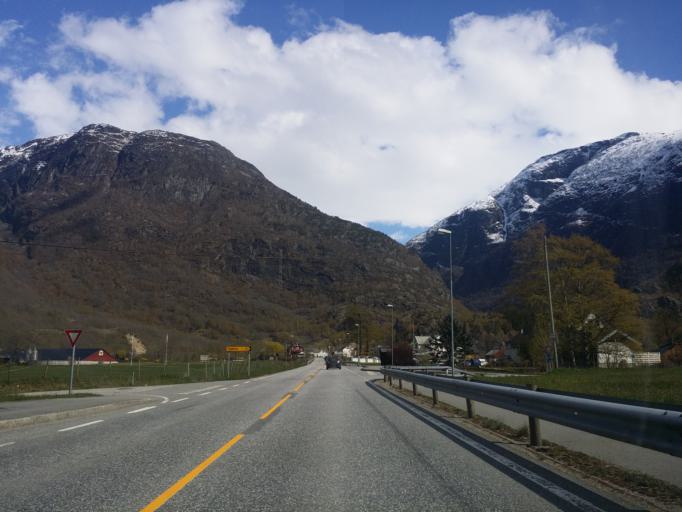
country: NO
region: Hordaland
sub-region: Eidfjord
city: Eidfjord
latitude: 60.4244
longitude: 7.1200
